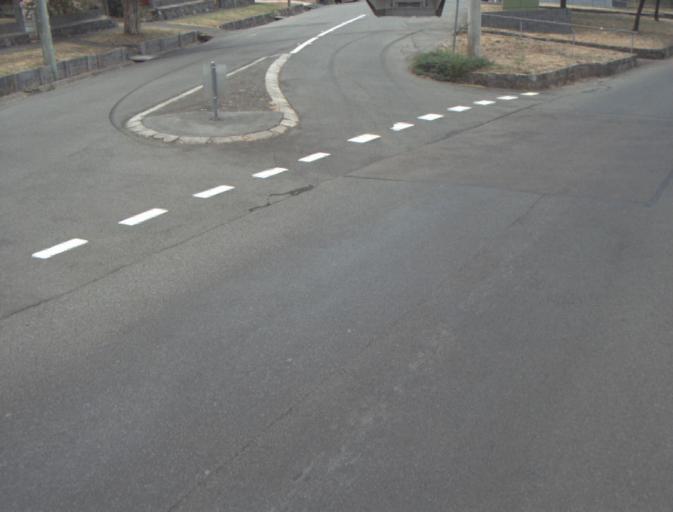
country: AU
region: Tasmania
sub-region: Launceston
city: West Launceston
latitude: -41.4481
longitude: 147.1329
